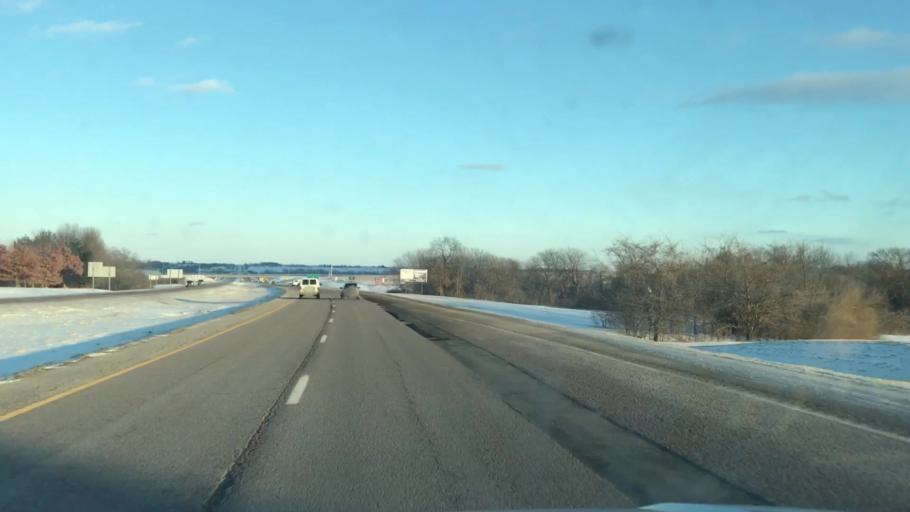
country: US
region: Missouri
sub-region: Buchanan County
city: Saint Joseph
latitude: 39.7481
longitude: -94.7617
